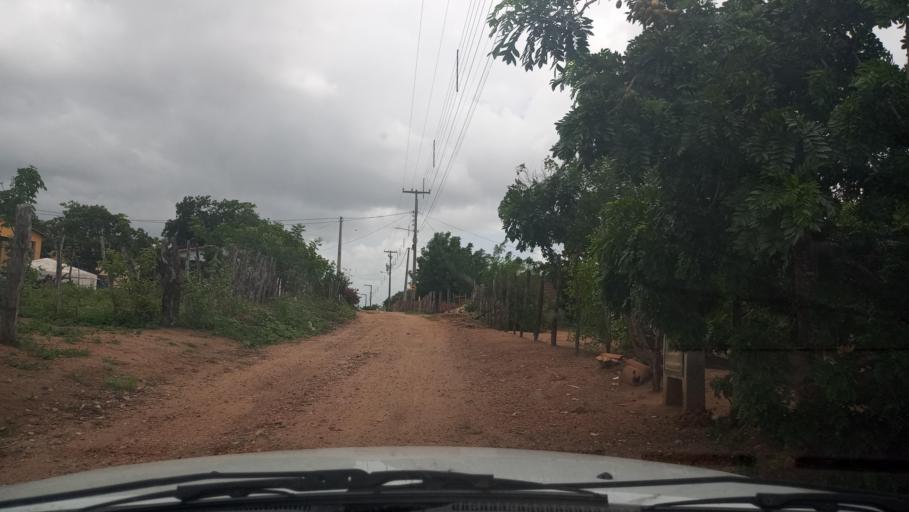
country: BR
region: Rio Grande do Norte
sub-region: Sao Paulo Do Potengi
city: Sao Paulo do Potengi
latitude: -5.9163
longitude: -35.6945
